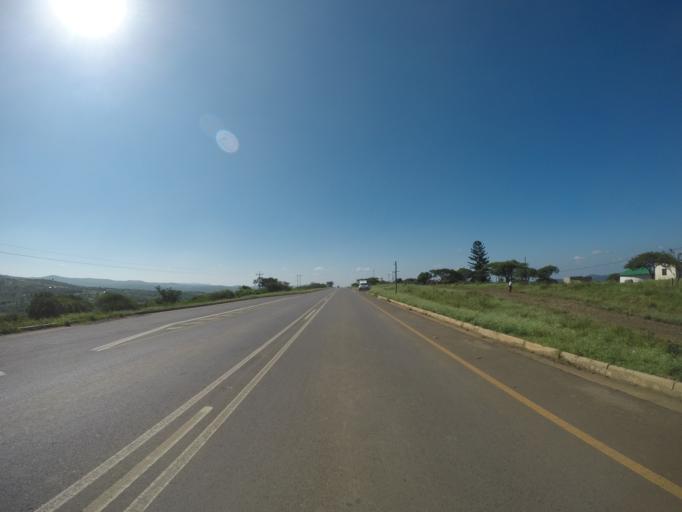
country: ZA
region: KwaZulu-Natal
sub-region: uThungulu District Municipality
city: Empangeni
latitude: -28.5679
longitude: 31.7096
